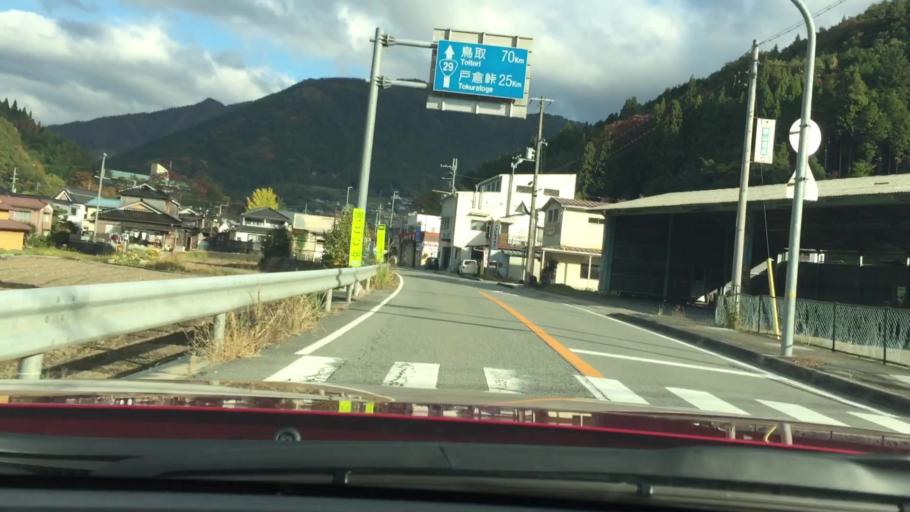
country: JP
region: Hyogo
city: Yamazakicho-nakabirose
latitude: 35.1668
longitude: 134.5445
